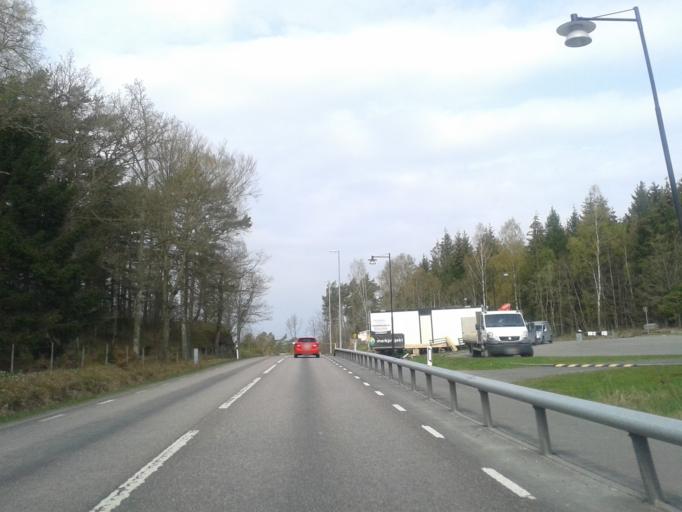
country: SE
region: Vaestra Goetaland
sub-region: Kungalvs Kommun
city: Kode
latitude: 57.8956
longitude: 11.8253
